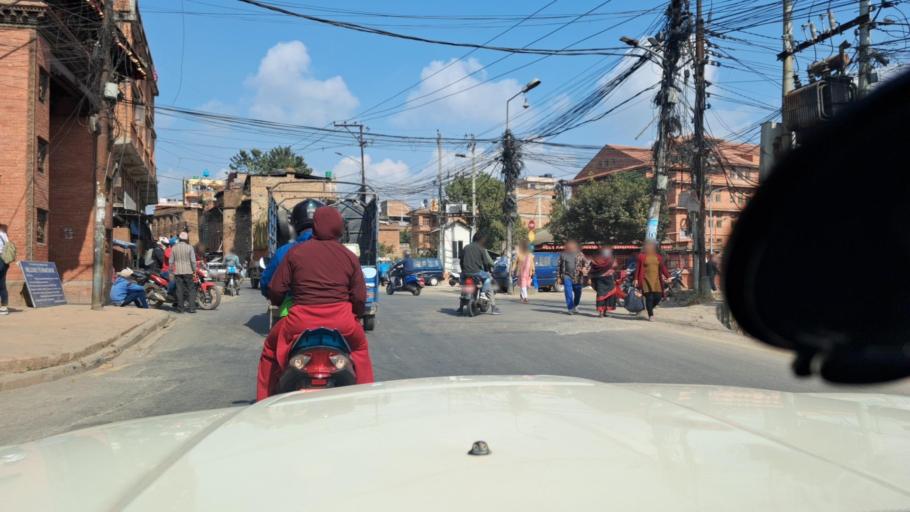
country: NP
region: Central Region
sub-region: Bagmati Zone
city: Bhaktapur
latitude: 27.6733
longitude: 85.4383
